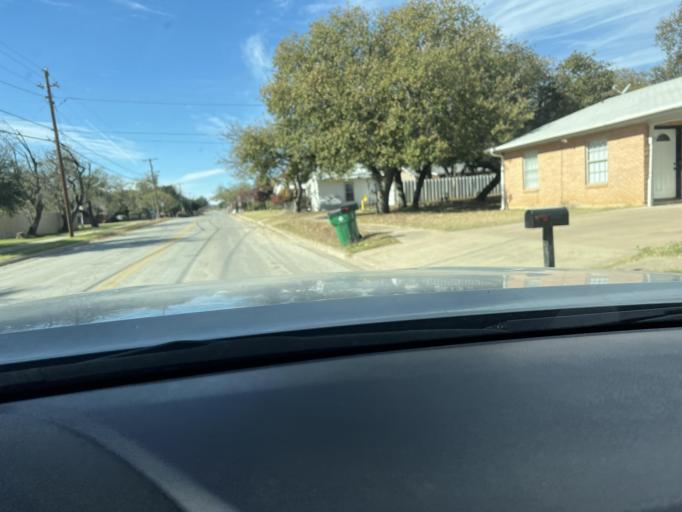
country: US
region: Texas
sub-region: Eastland County
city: Eastland
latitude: 32.3955
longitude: -98.8244
